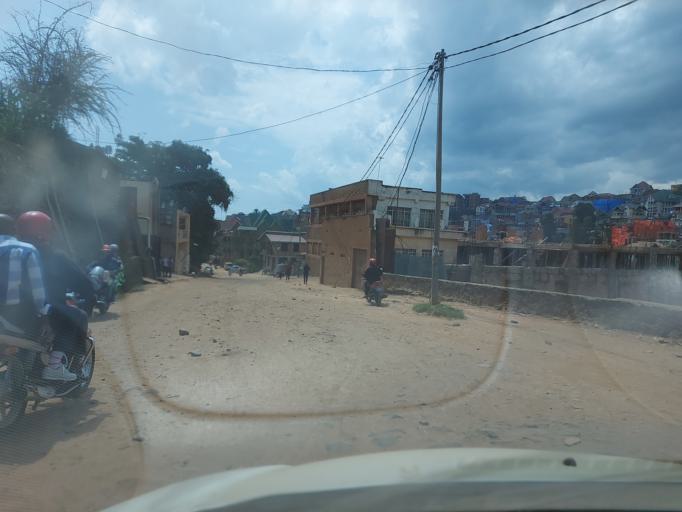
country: CD
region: South Kivu
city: Bukavu
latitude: -2.5038
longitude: 28.8618
